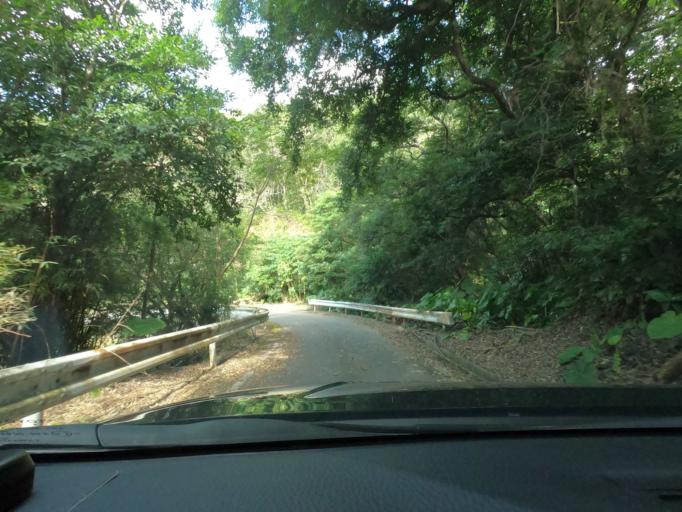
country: JP
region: Okinawa
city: Nago
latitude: 26.7573
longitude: 128.1975
